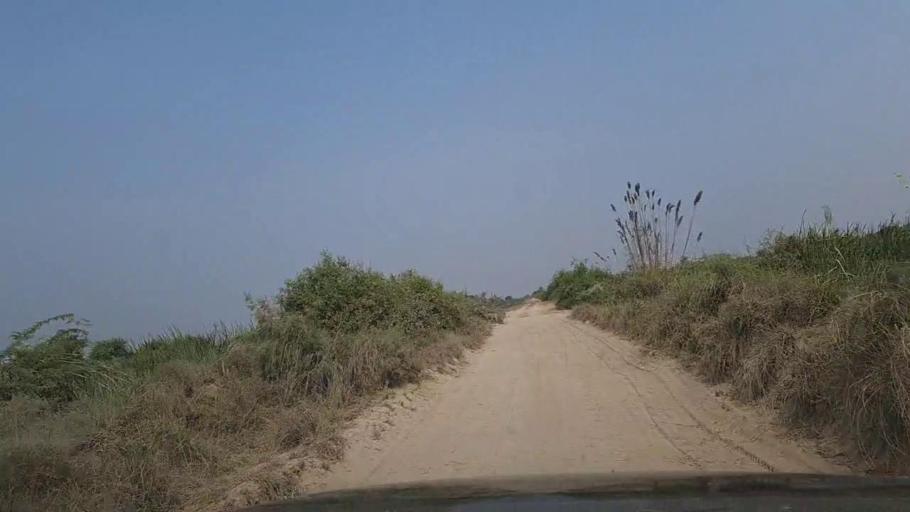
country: PK
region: Sindh
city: Thatta
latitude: 24.7516
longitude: 67.8085
